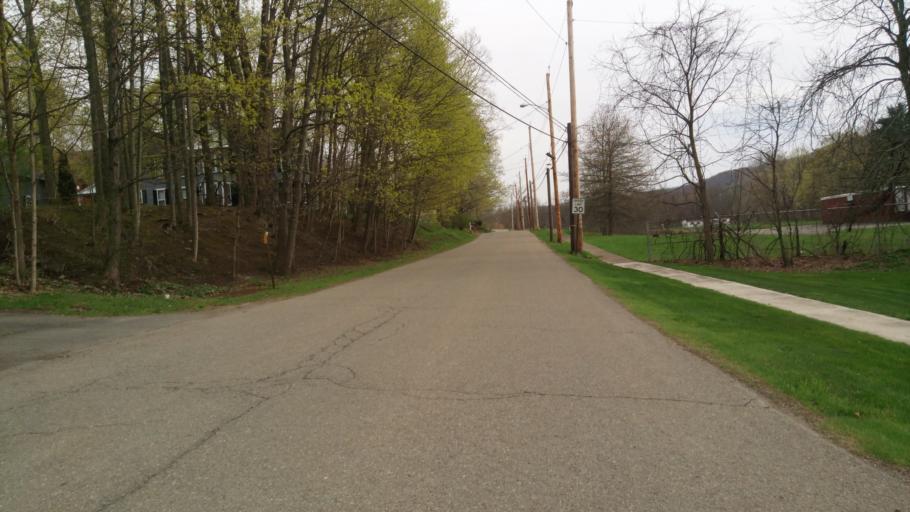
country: US
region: New York
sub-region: Chemung County
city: Southport
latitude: 42.0131
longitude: -76.7262
